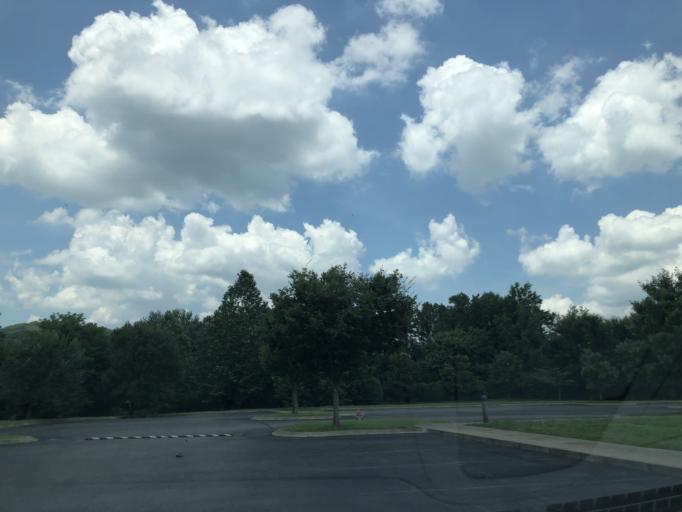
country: US
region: Tennessee
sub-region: Williamson County
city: Brentwood Estates
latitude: 36.0226
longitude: -86.7149
